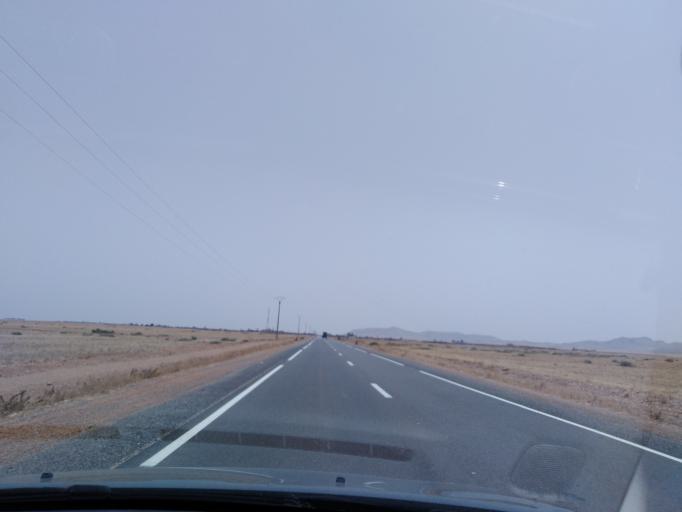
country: MA
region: Doukkala-Abda
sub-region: Safi
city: Youssoufia
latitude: 31.9738
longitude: -8.3235
